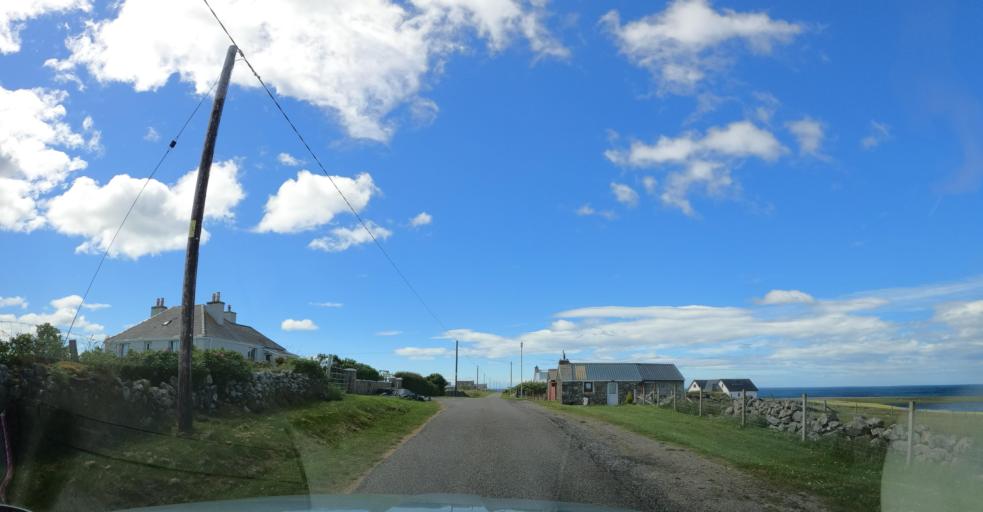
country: GB
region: Scotland
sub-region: Eilean Siar
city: Isle of Lewis
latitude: 58.3569
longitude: -6.5560
